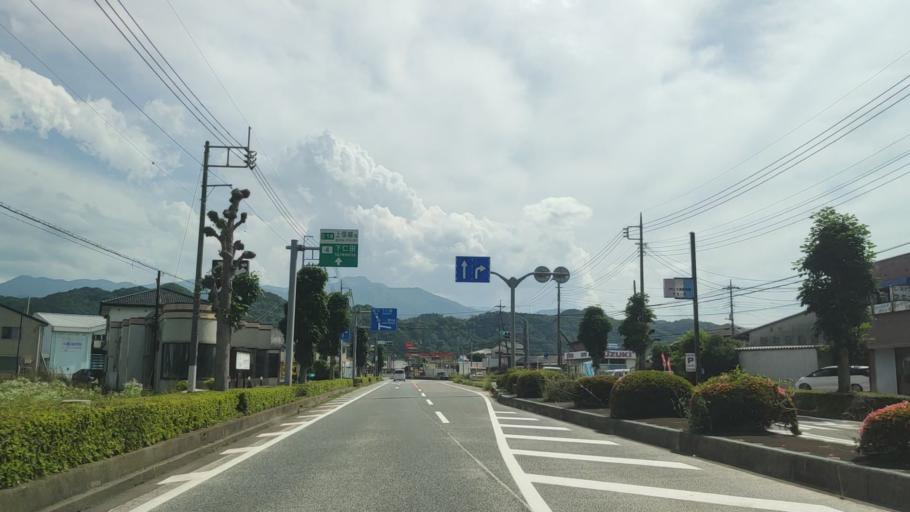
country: JP
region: Gunma
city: Tomioka
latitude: 36.2484
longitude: 138.8597
